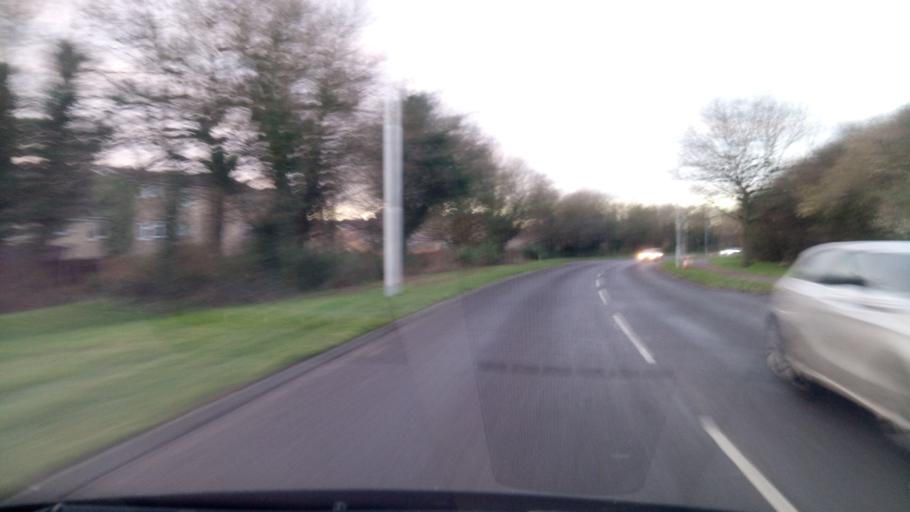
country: GB
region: England
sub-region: Peterborough
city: Marholm
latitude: 52.5799
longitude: -0.2884
